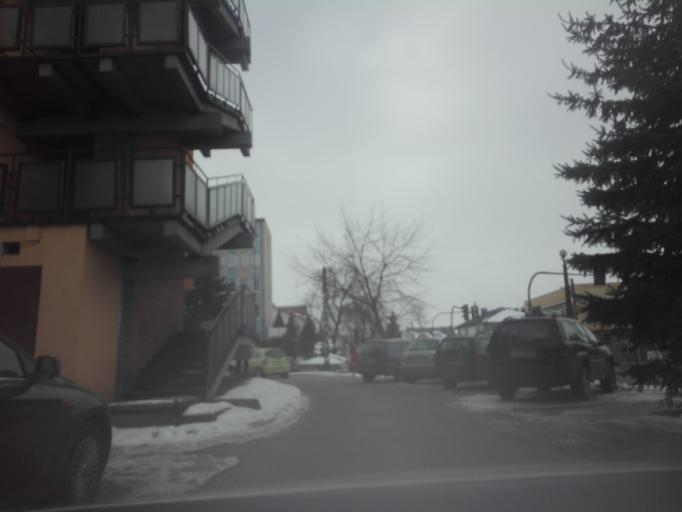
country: PL
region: Lublin Voivodeship
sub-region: Powiat hrubieszowski
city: Hrubieszow
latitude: 50.8030
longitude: 23.8965
